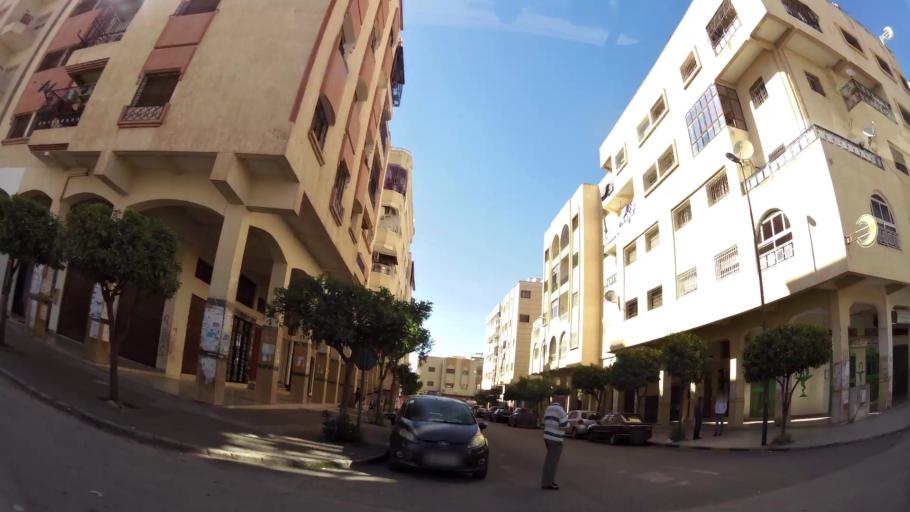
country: MA
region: Fes-Boulemane
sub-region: Fes
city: Fes
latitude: 34.0111
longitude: -4.9767
